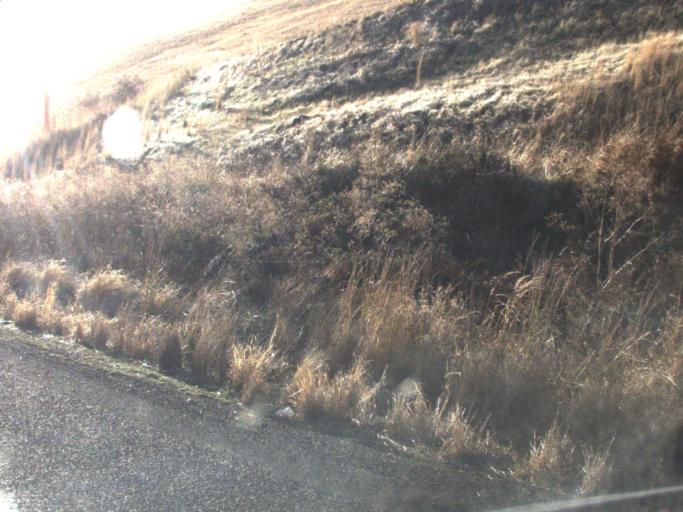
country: US
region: Washington
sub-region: Walla Walla County
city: Waitsburg
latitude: 46.1565
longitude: -118.1334
